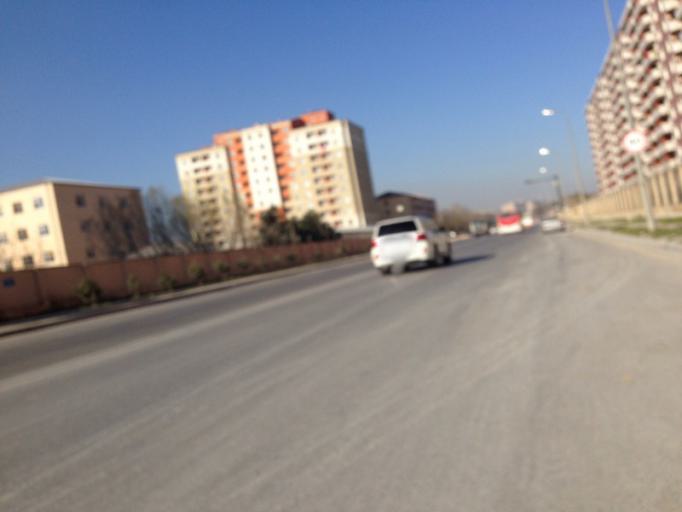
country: AZ
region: Baki
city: Baku
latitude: 40.4135
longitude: 49.8705
